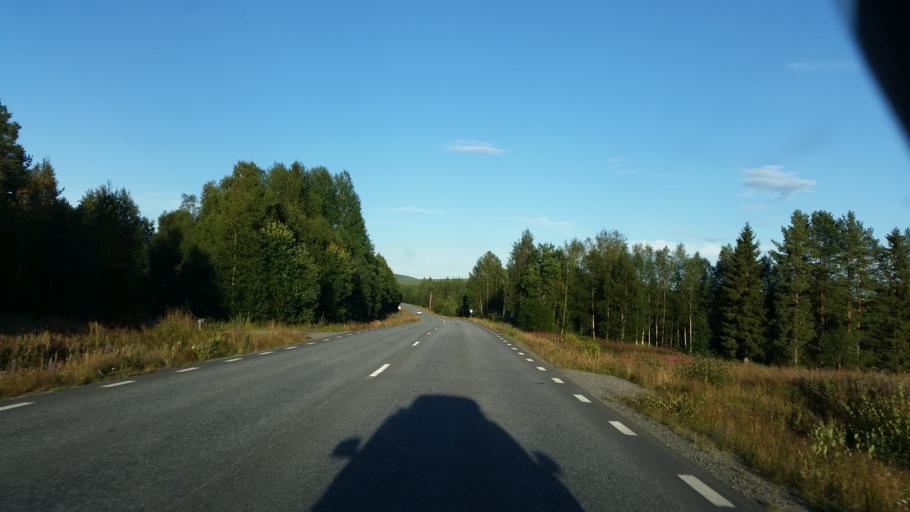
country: SE
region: Vaesterbotten
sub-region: Dorotea Kommun
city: Dorotea
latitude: 64.2548
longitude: 16.4559
